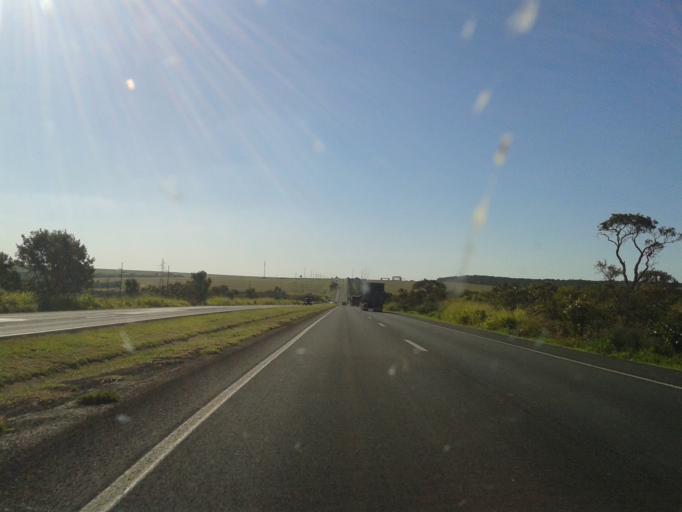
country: BR
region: Minas Gerais
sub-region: Uberlandia
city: Uberlandia
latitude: -19.0993
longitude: -48.1817
